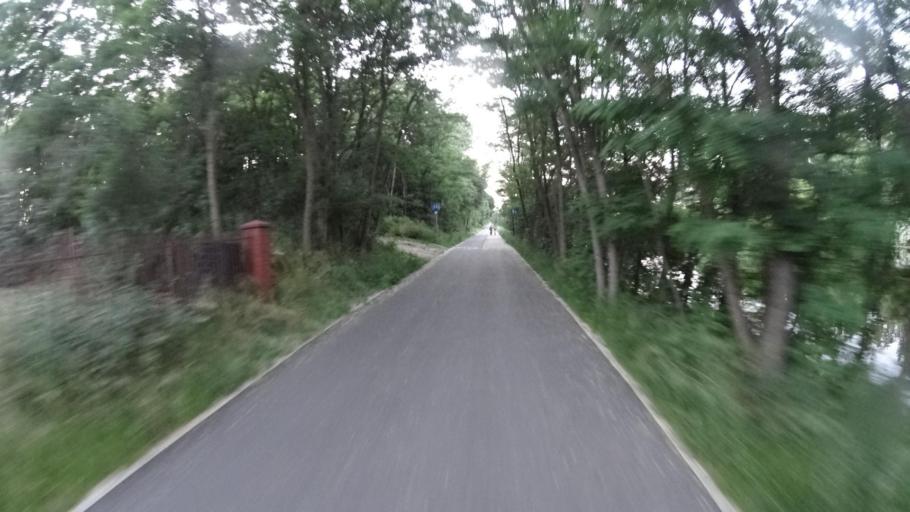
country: PL
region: Masovian Voivodeship
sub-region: Powiat legionowski
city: Stanislawow Pierwszy
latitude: 52.3765
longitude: 21.0346
